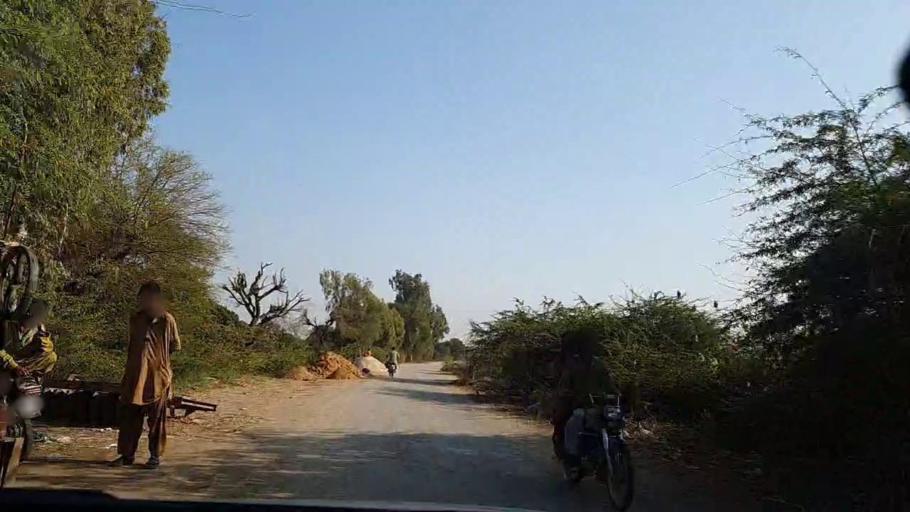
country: PK
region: Sindh
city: Tando Ghulam Ali
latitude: 25.2233
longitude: 68.9445
